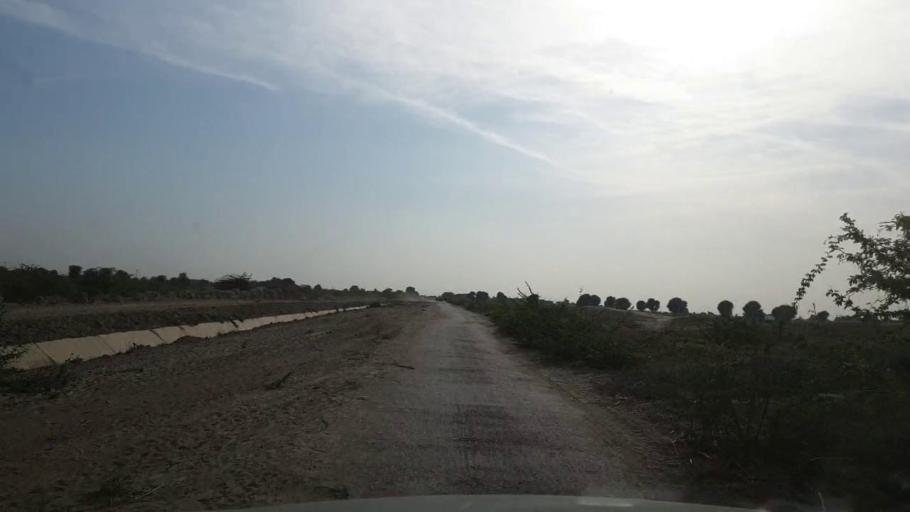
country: PK
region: Sindh
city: Kunri
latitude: 25.1571
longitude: 69.5134
